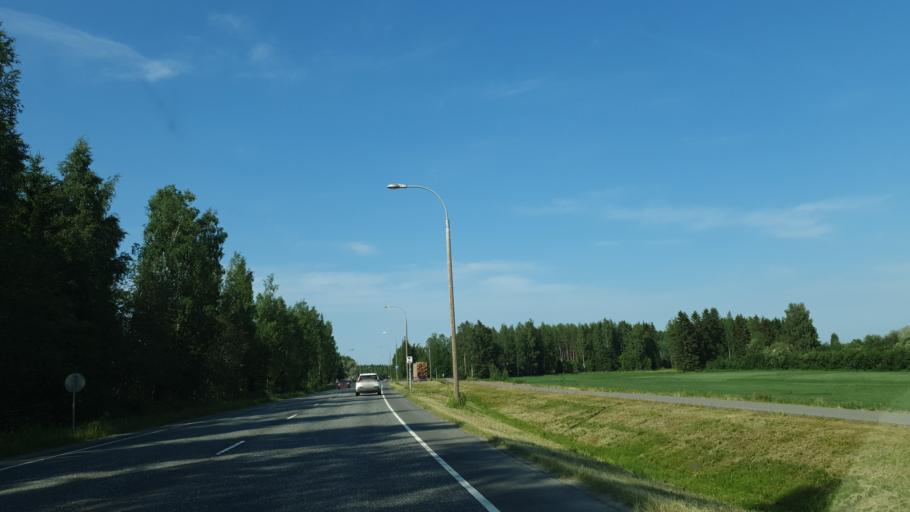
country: FI
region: Northern Savo
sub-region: Kuopio
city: Siilinjaervi
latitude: 63.1237
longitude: 27.7697
